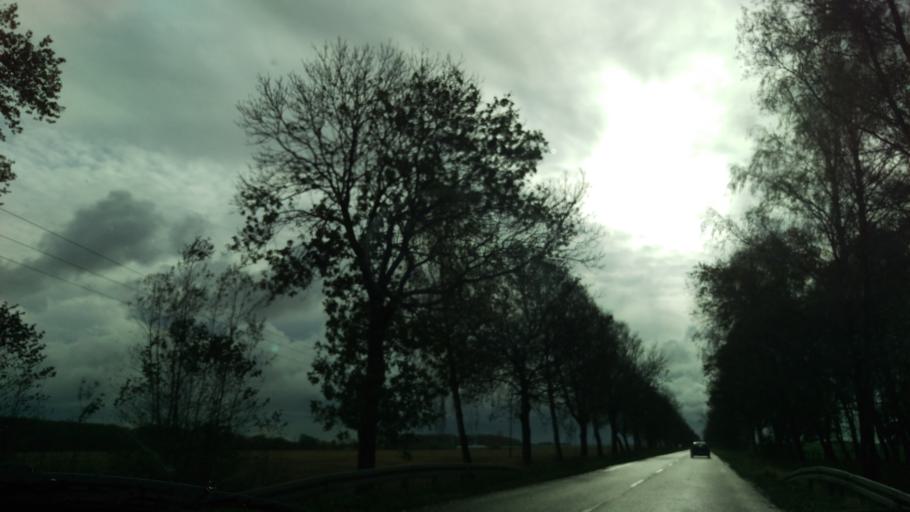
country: PL
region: West Pomeranian Voivodeship
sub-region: Powiat gryficki
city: Gryfice
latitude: 53.8817
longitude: 15.2115
